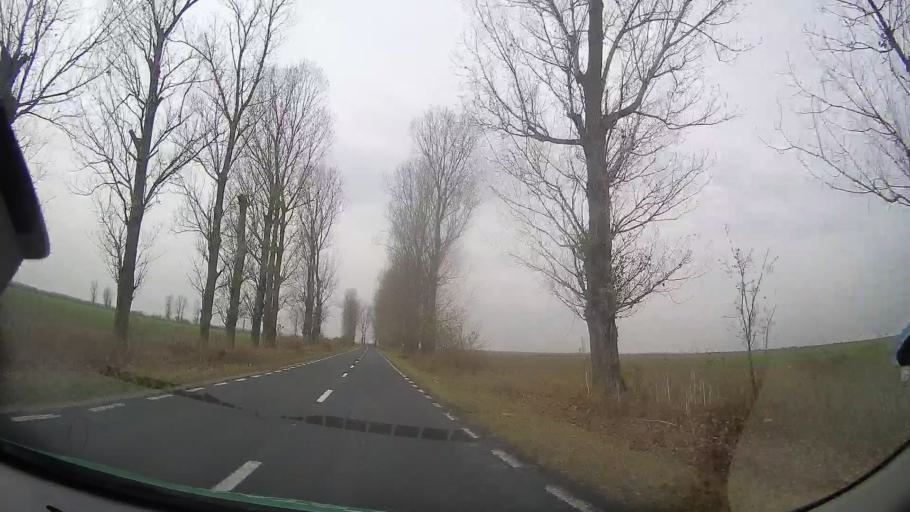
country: RO
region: Ilfov
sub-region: Comuna Gruiu
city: Lipia
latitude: 44.7232
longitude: 26.2759
